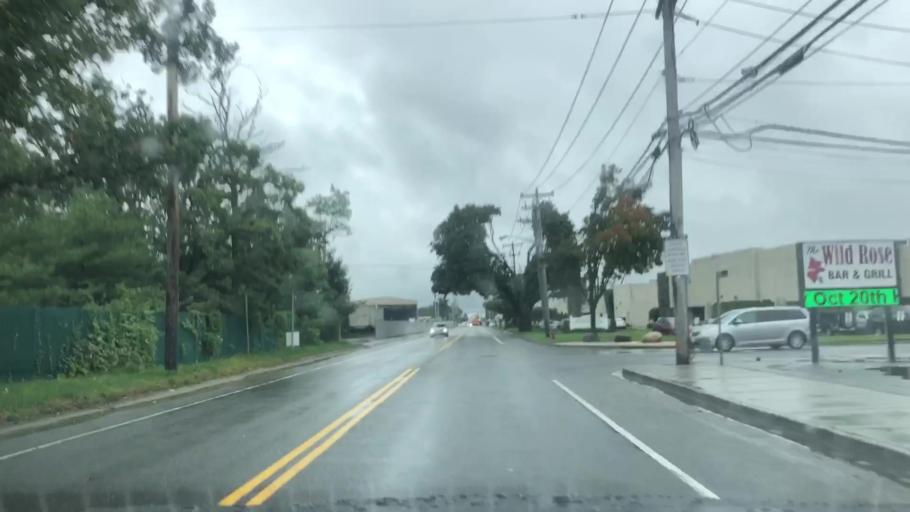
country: US
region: New York
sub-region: Suffolk County
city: East Farmingdale
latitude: 40.7461
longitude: -73.4140
